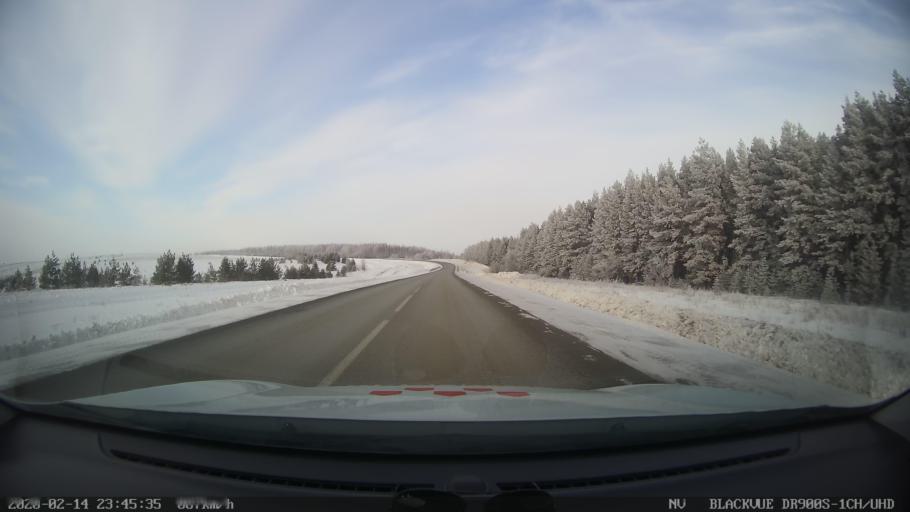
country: RU
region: Tatarstan
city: Kuybyshevskiy Zaton
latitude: 55.2227
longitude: 49.2328
